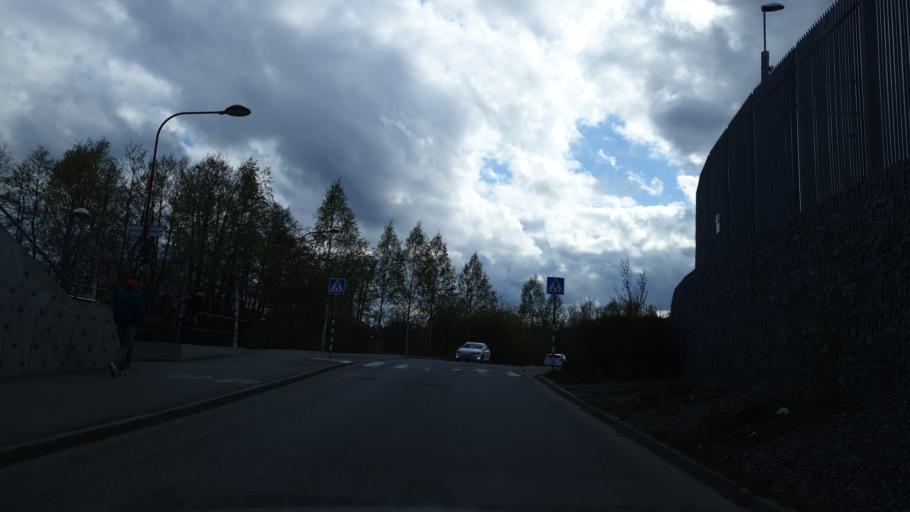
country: SE
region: Stockholm
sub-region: Sundbybergs Kommun
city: Sundbyberg
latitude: 59.3429
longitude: 17.9692
